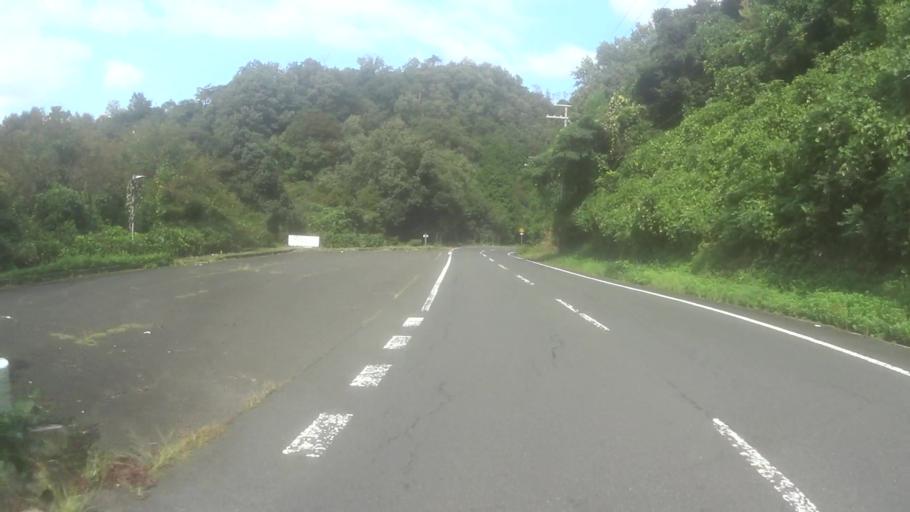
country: JP
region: Kyoto
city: Miyazu
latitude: 35.5888
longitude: 135.1180
